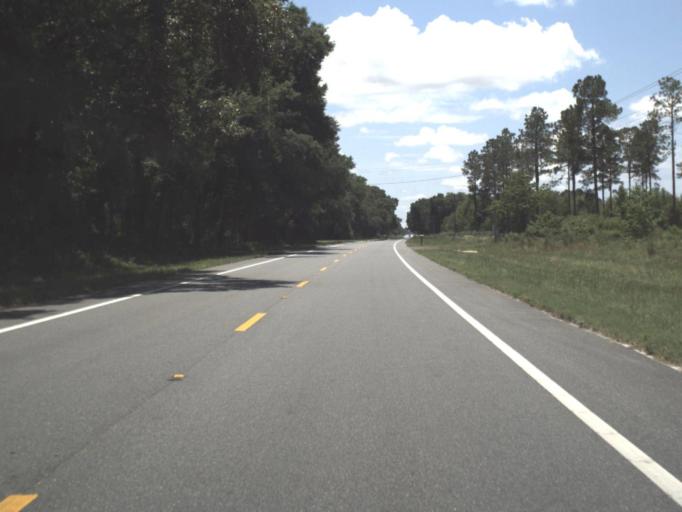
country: US
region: Florida
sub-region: Lafayette County
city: Mayo
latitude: 29.9384
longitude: -82.9488
